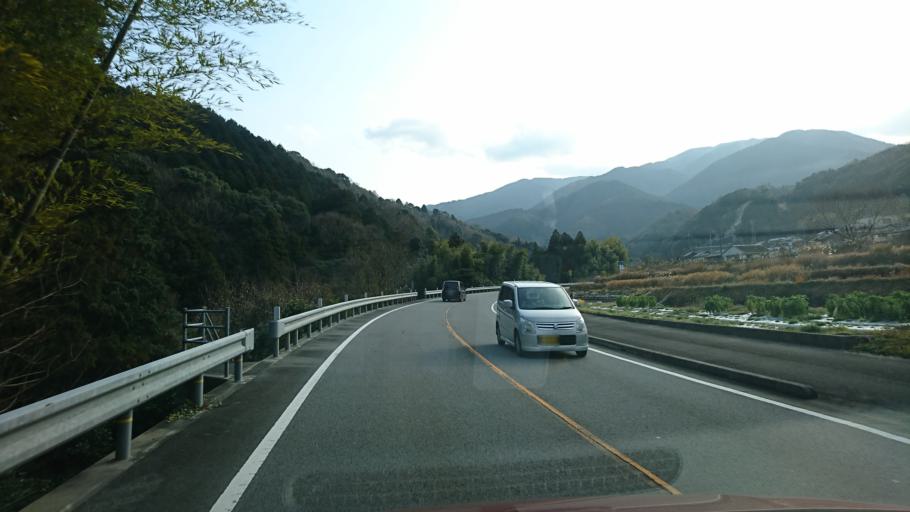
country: JP
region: Ehime
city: Hojo
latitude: 33.9787
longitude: 132.9050
